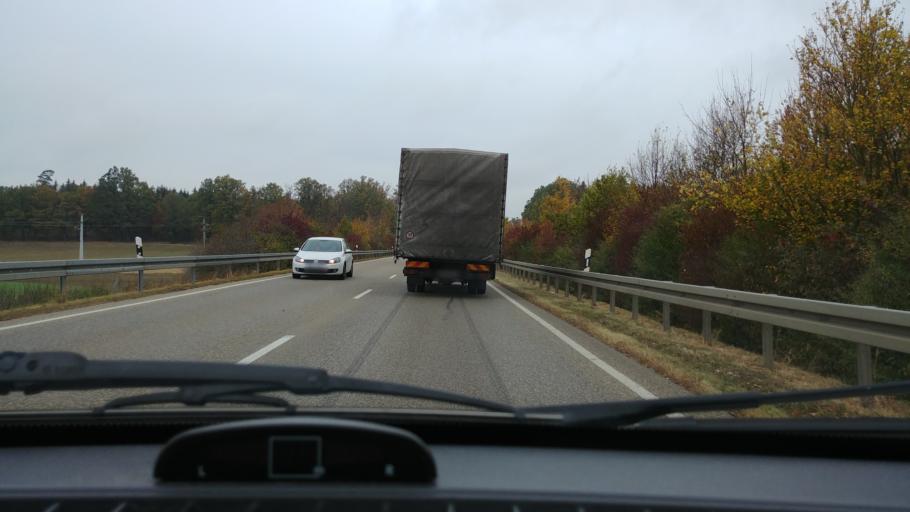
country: DE
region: Baden-Wuerttemberg
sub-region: Regierungsbezirk Stuttgart
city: Aalen
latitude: 48.8499
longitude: 10.0701
